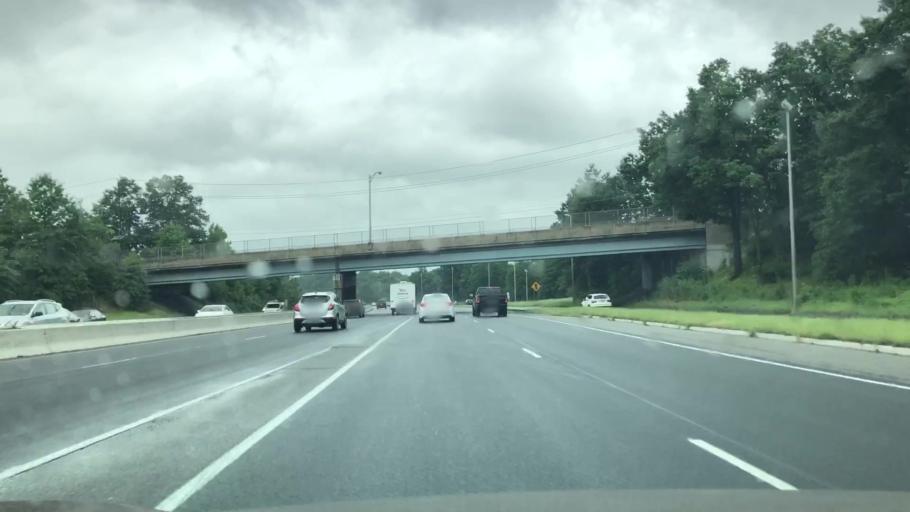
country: US
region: New Jersey
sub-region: Middlesex County
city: Fords
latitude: 40.5225
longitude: -74.3093
